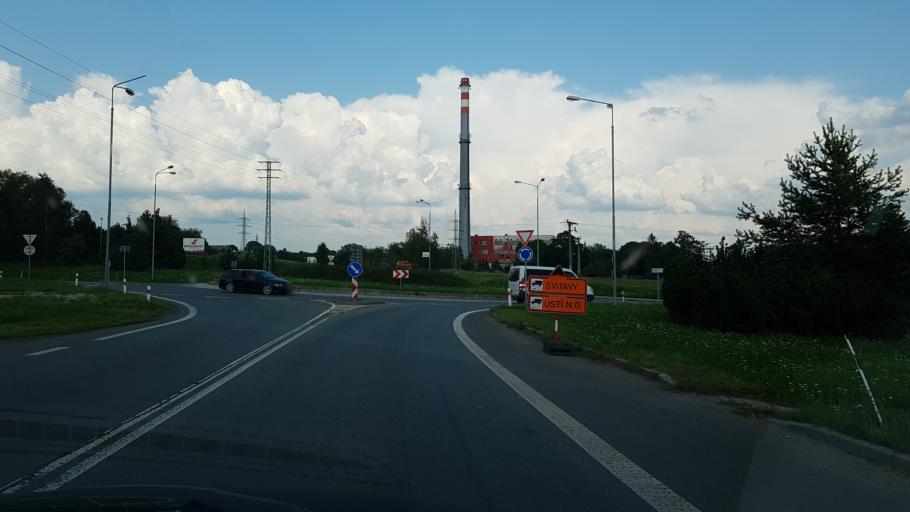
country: CZ
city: Vamberk
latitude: 50.1209
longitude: 16.2830
